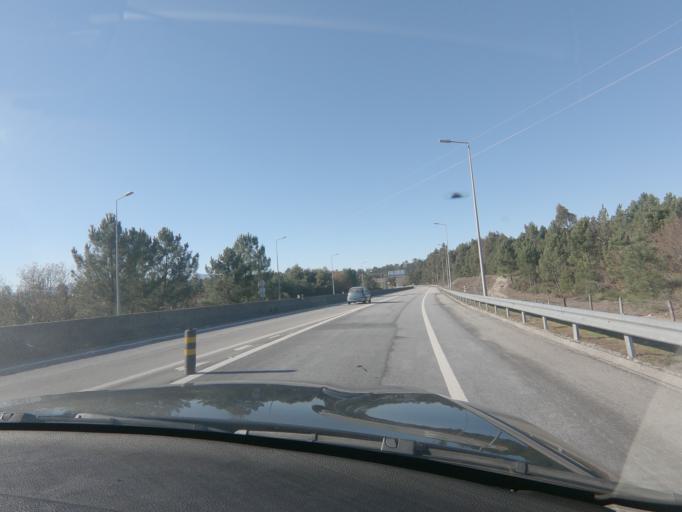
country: PT
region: Viseu
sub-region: Viseu
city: Abraveses
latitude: 40.6736
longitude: -7.9744
